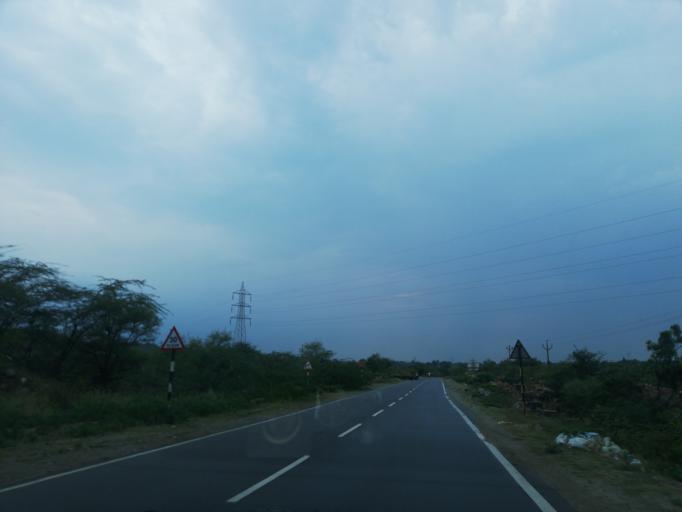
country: IN
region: Andhra Pradesh
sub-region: Guntur
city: Macherla
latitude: 16.6661
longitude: 79.2837
